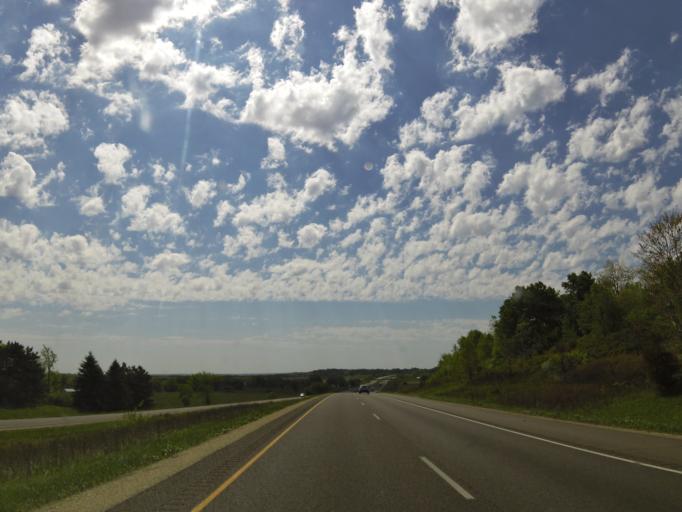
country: US
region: Wisconsin
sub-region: Eau Claire County
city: Eau Claire
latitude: 44.8290
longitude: -91.5767
